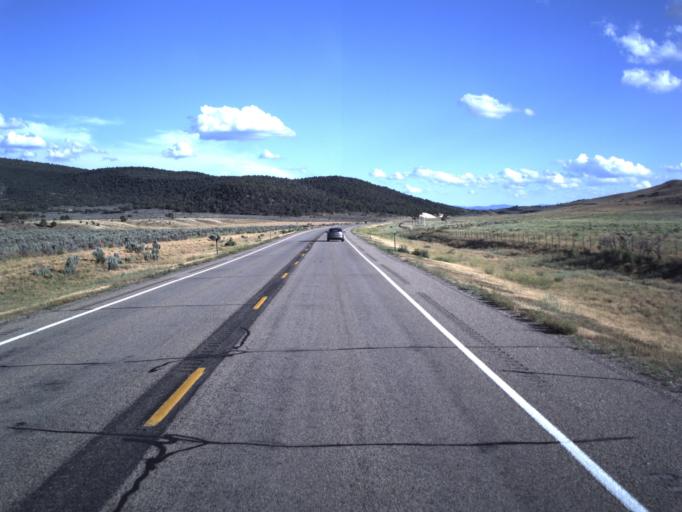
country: US
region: Utah
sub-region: Sanpete County
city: Fairview
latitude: 39.7588
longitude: -111.4819
